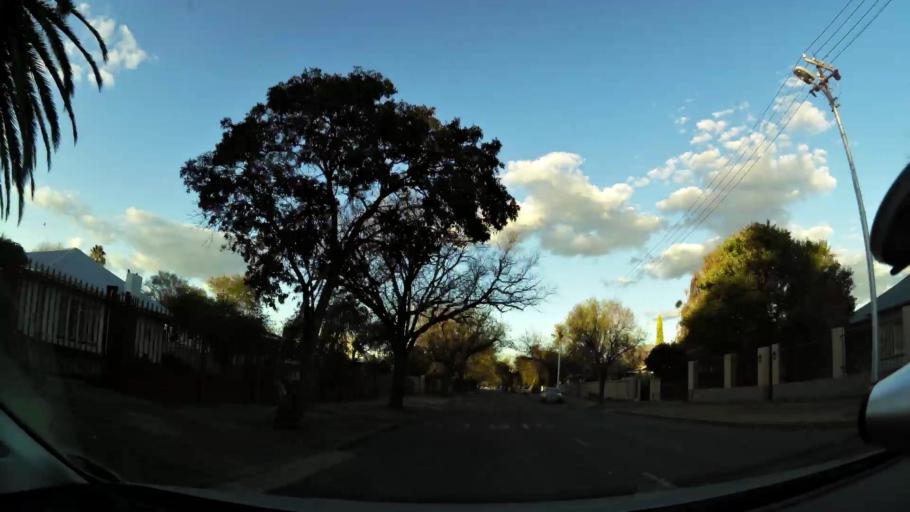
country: ZA
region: North-West
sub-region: Dr Kenneth Kaunda District Municipality
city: Potchefstroom
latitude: -26.7210
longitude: 27.0989
